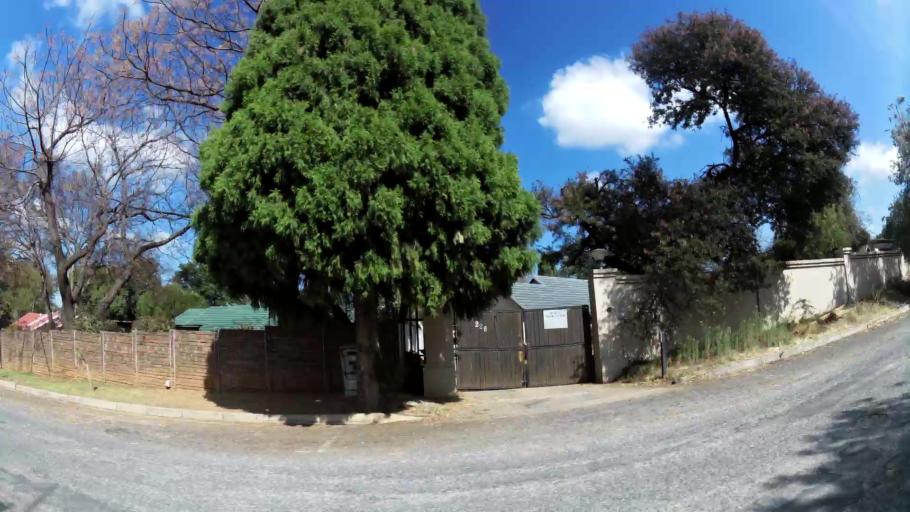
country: ZA
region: Gauteng
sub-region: West Rand District Municipality
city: Muldersdriseloop
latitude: -26.0619
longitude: 27.9609
